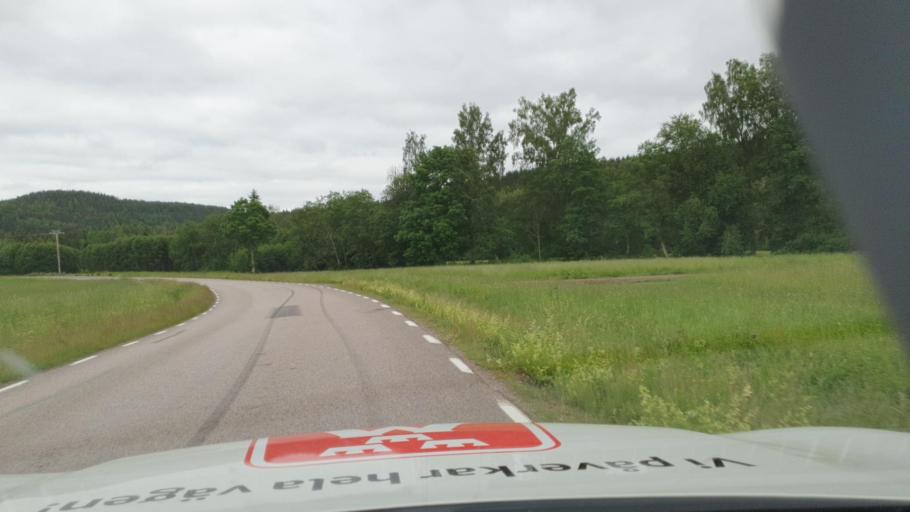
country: SE
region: Vaermland
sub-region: Kils Kommun
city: Kil
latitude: 59.6876
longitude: 13.2644
